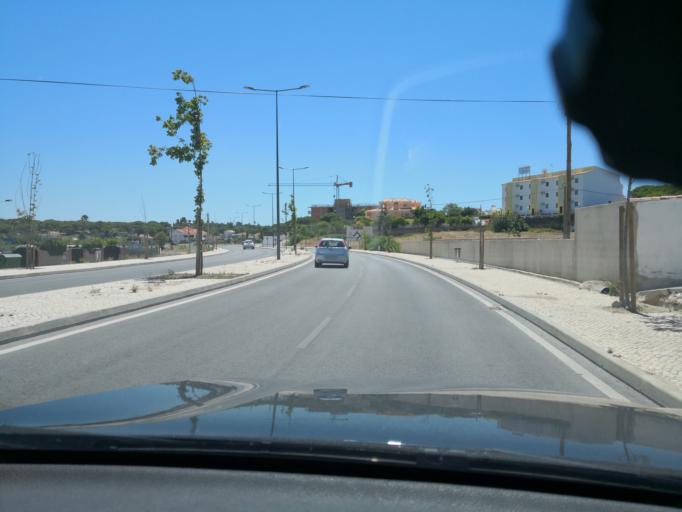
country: PT
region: Faro
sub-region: Loule
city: Quarteira
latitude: 37.0714
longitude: -8.0870
